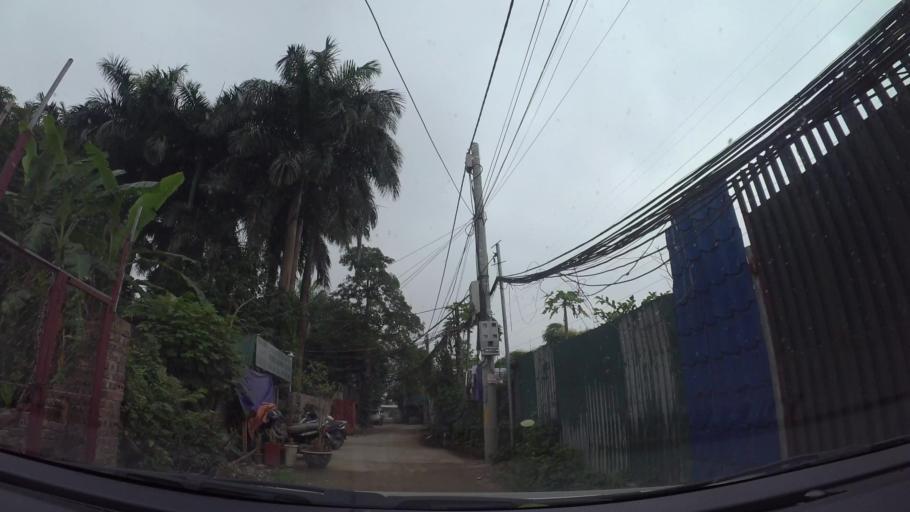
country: VN
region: Ha Noi
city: Tay Ho
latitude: 21.0709
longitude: 105.8306
